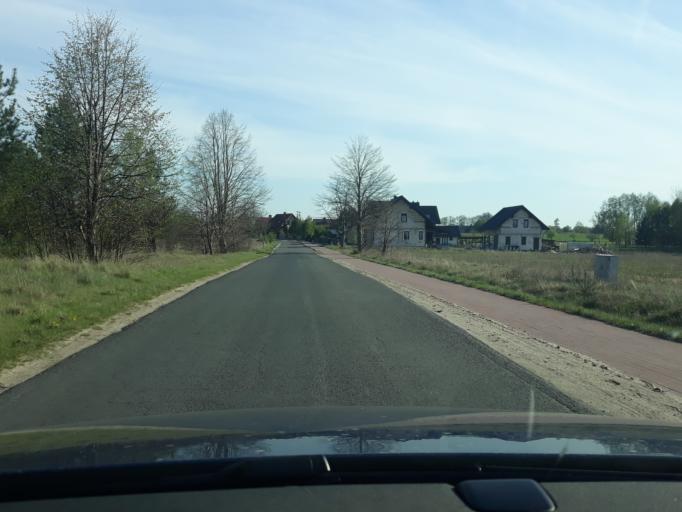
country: PL
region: Pomeranian Voivodeship
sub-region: Powiat czluchowski
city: Przechlewo
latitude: 53.8292
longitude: 17.3769
